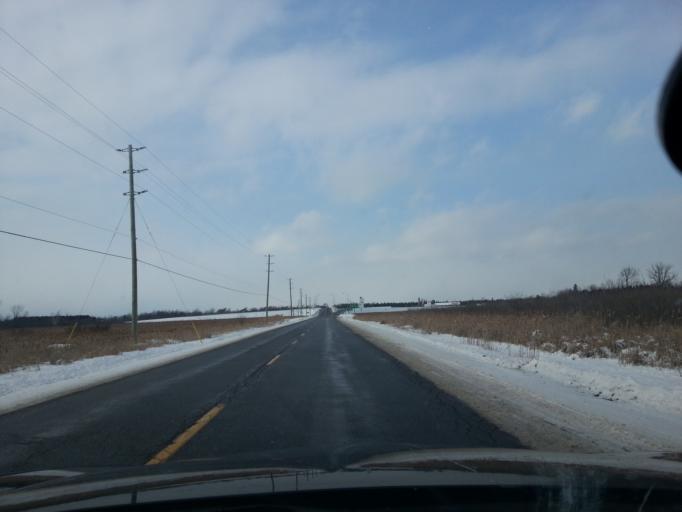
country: CA
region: Ontario
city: Carleton Place
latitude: 45.1664
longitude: -76.0442
